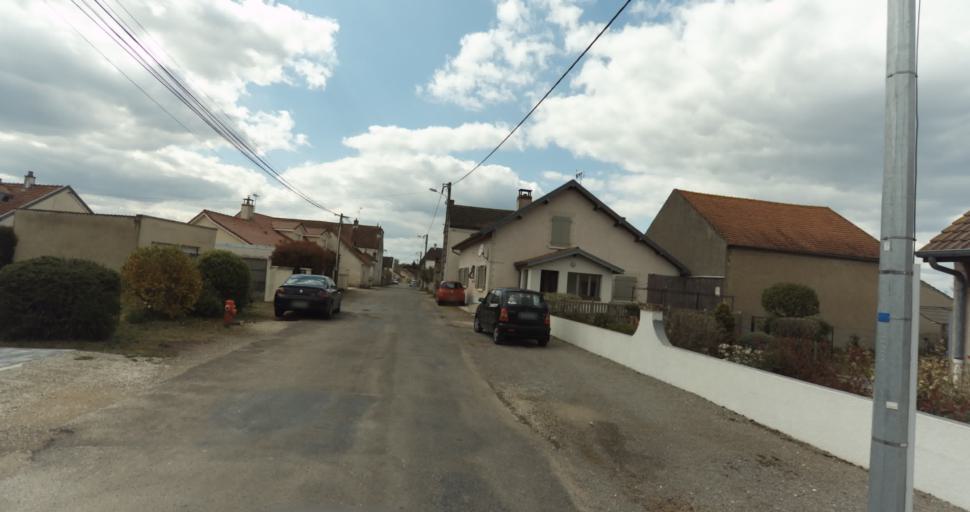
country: FR
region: Bourgogne
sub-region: Departement de la Cote-d'Or
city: Auxonne
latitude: 47.1839
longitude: 5.3901
